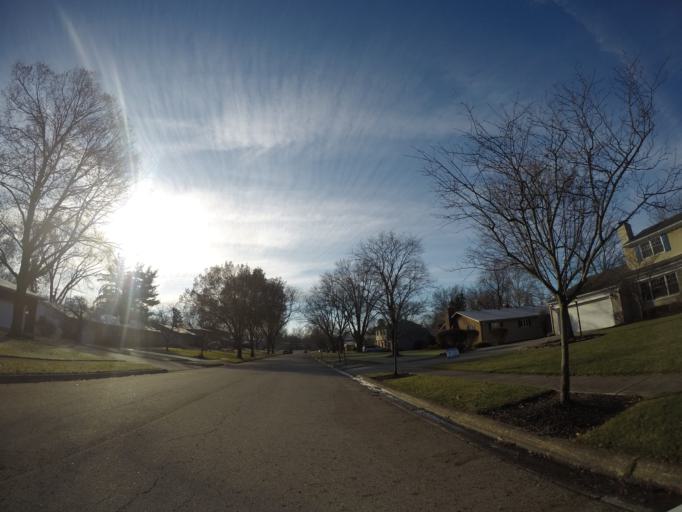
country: US
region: Ohio
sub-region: Franklin County
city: Upper Arlington
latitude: 40.0444
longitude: -83.0824
